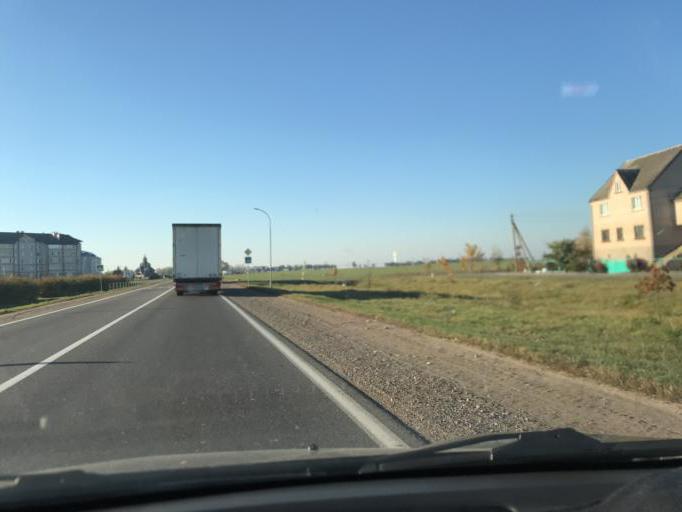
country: BY
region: Minsk
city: Slutsk
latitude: 53.0460
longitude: 27.5711
